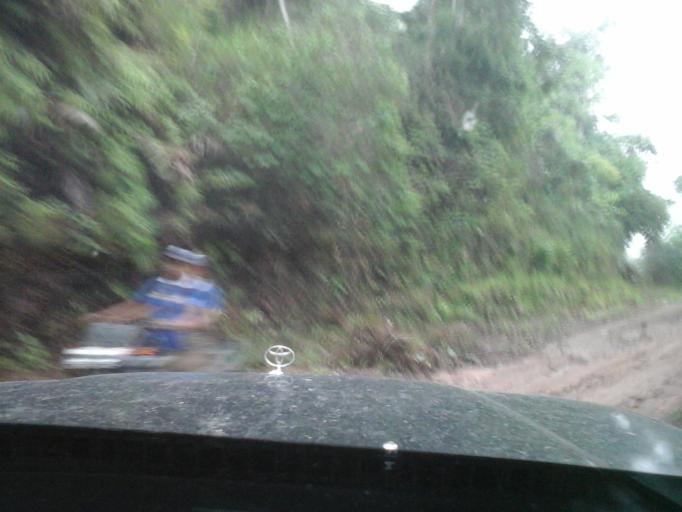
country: CO
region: Cesar
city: Agustin Codazzi
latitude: 9.9386
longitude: -73.1404
